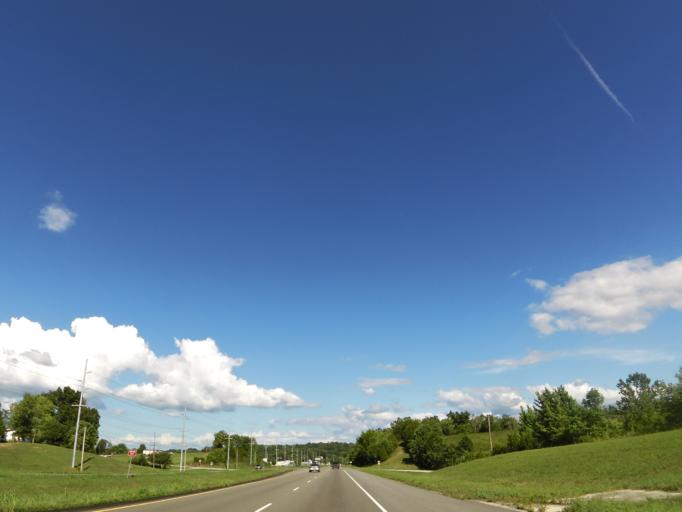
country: US
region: Tennessee
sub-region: Greene County
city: Mosheim
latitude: 36.1869
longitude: -82.9454
